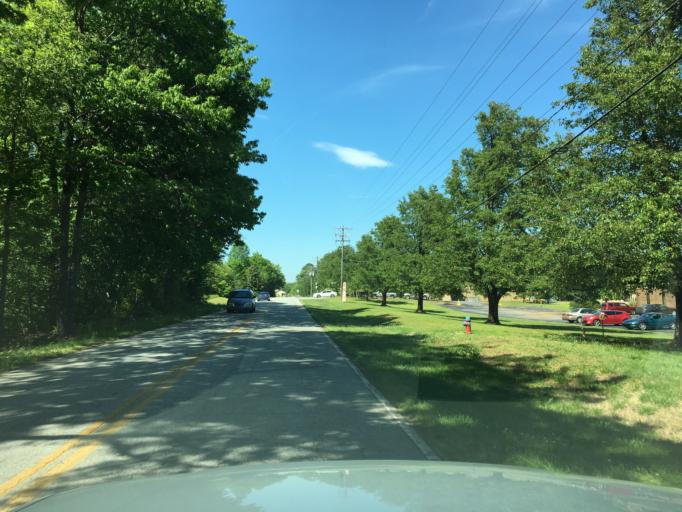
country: US
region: South Carolina
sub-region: Spartanburg County
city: Fairforest
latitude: 34.9774
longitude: -82.0325
